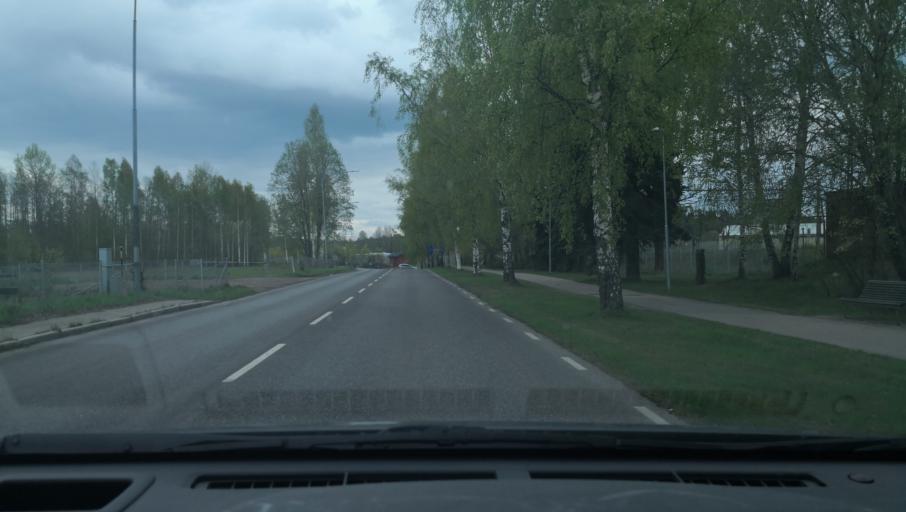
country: SE
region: Dalarna
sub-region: Avesta Kommun
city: Avesta
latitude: 60.1264
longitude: 16.2186
